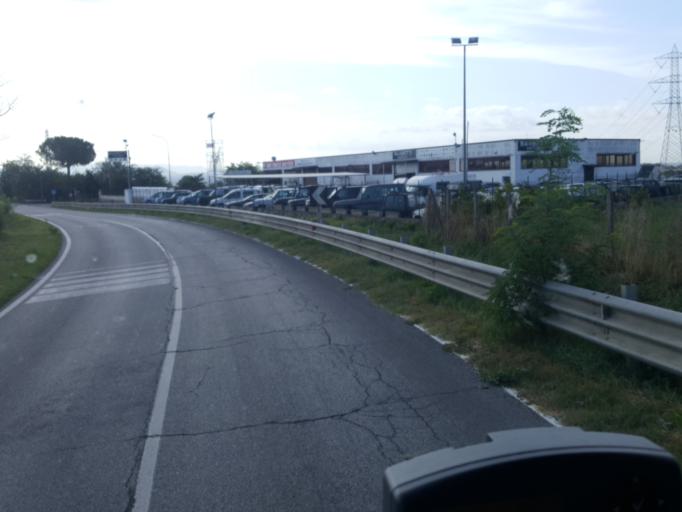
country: IT
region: Latium
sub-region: Citta metropolitana di Roma Capitale
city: Bivio di Capanelle
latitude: 42.1252
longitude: 12.5760
